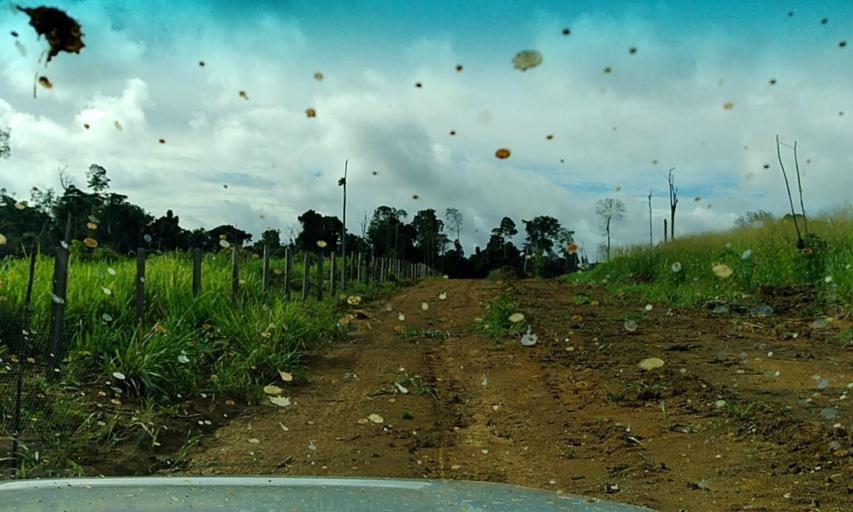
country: BR
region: Para
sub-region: Senador Jose Porfirio
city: Senador Jose Porfirio
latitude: -3.0002
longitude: -51.7406
